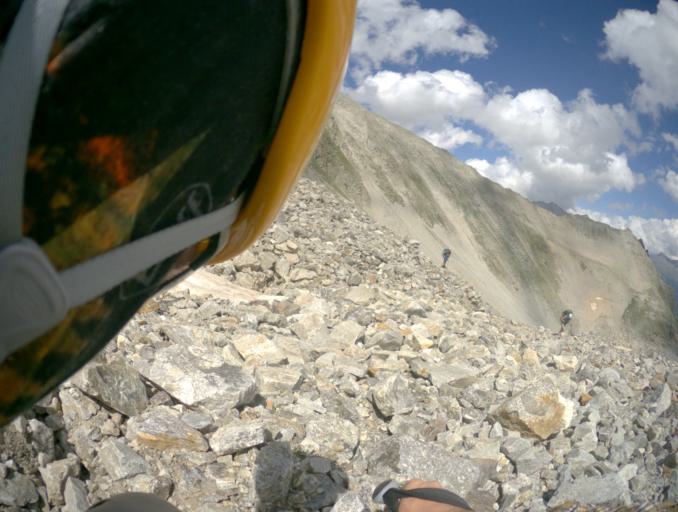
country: RU
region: Karachayevo-Cherkesiya
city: Uchkulan
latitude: 43.3209
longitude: 42.0811
